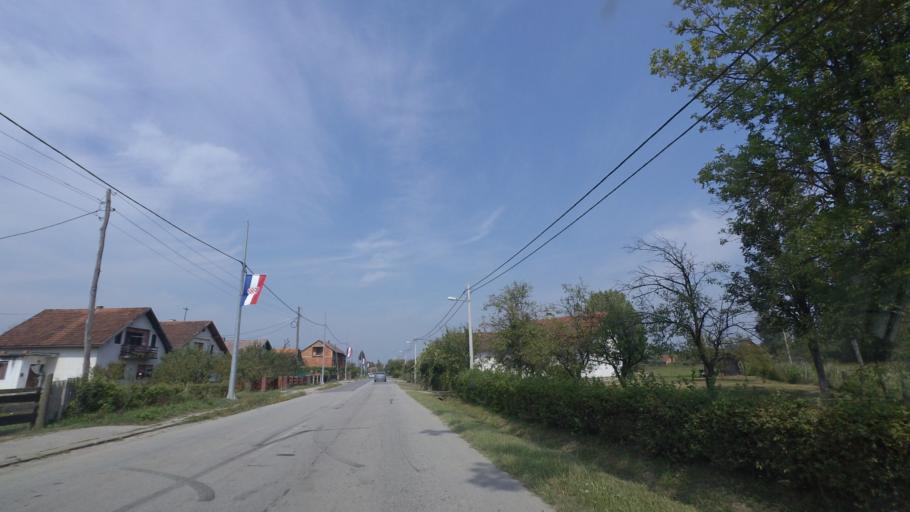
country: HR
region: Sisacko-Moslavacka
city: Glina
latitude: 45.3266
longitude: 16.1044
